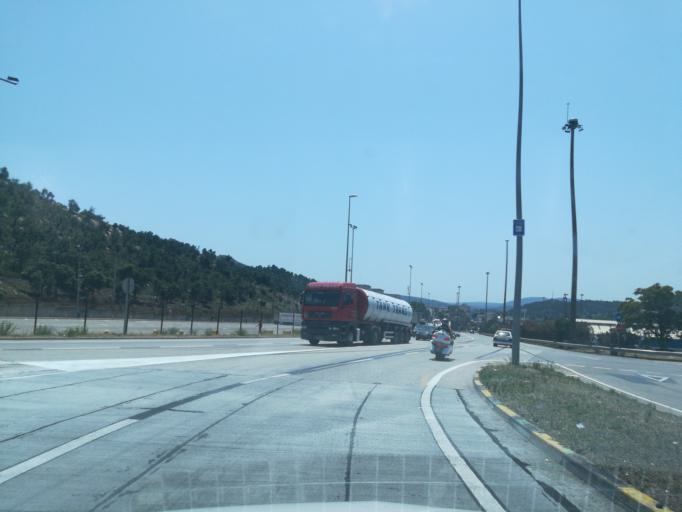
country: ES
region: Catalonia
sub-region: Provincia de Girona
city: la Jonquera
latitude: 42.4331
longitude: 2.8660
